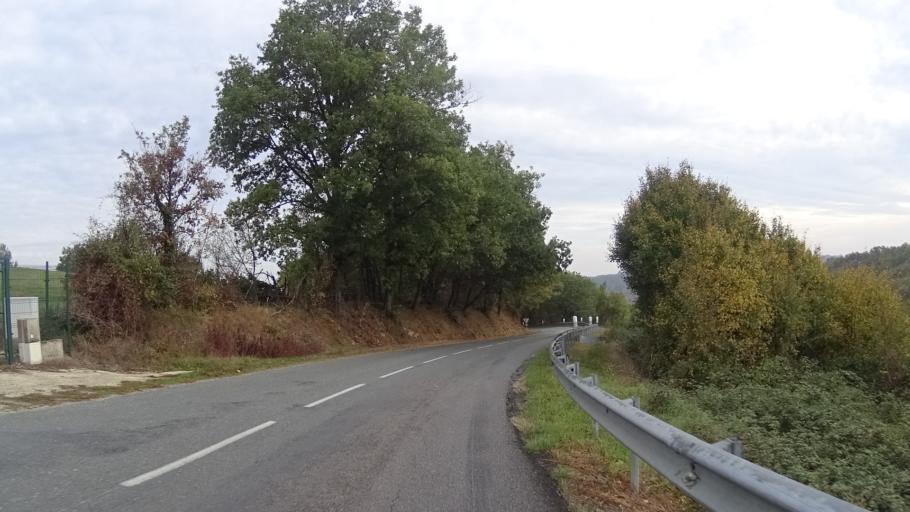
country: FR
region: Aquitaine
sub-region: Departement du Lot-et-Garonne
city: Boe
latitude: 44.1491
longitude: 0.6121
